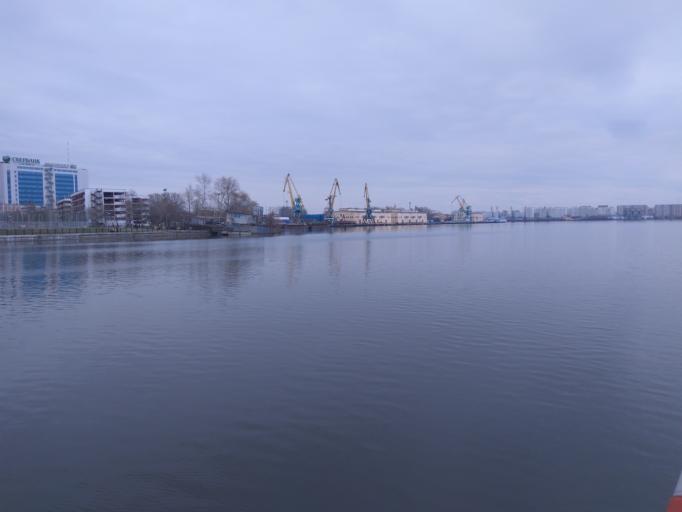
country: RU
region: Moskovskaya
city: Kozhukhovo
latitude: 55.6978
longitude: 37.6810
